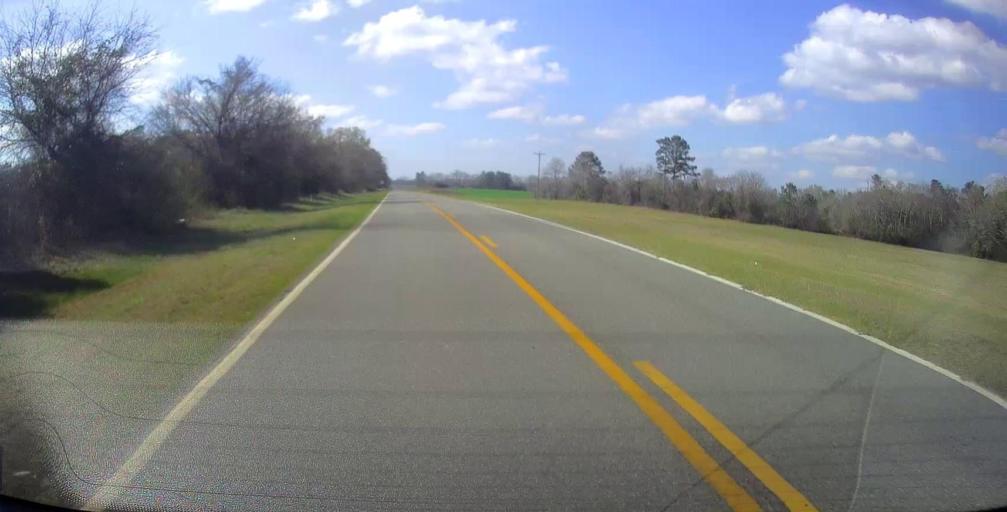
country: US
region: Georgia
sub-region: Wilkinson County
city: Irwinton
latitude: 32.6267
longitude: -83.0943
